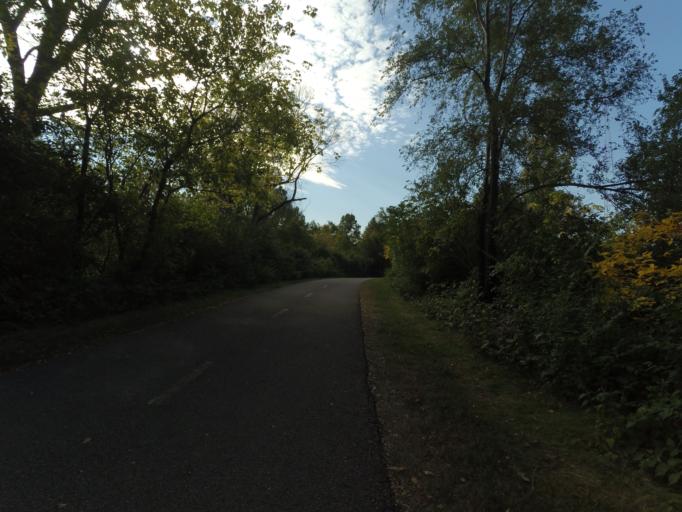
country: US
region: Ohio
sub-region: Franklin County
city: Grandview Heights
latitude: 39.9734
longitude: -83.0209
